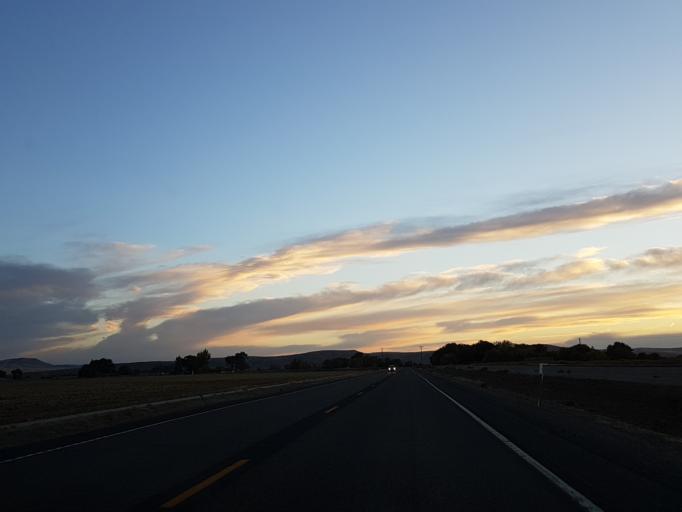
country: US
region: Oregon
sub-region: Malheur County
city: Vale
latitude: 43.9439
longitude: -117.3025
